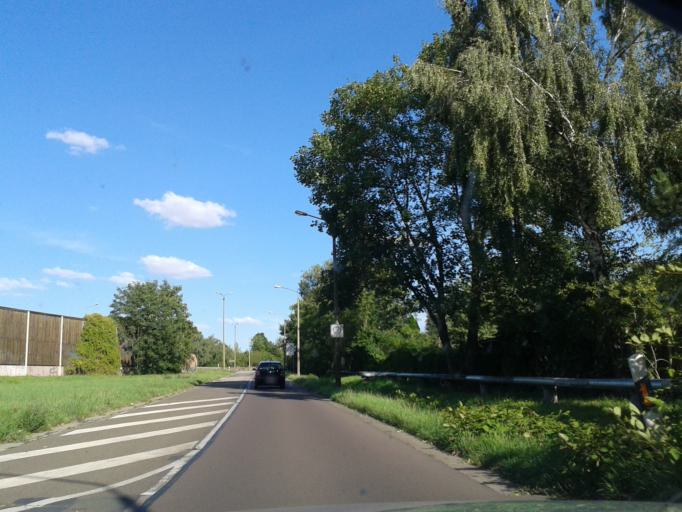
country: DE
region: Saxony-Anhalt
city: Halle (Saale)
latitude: 51.5013
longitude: 11.9737
